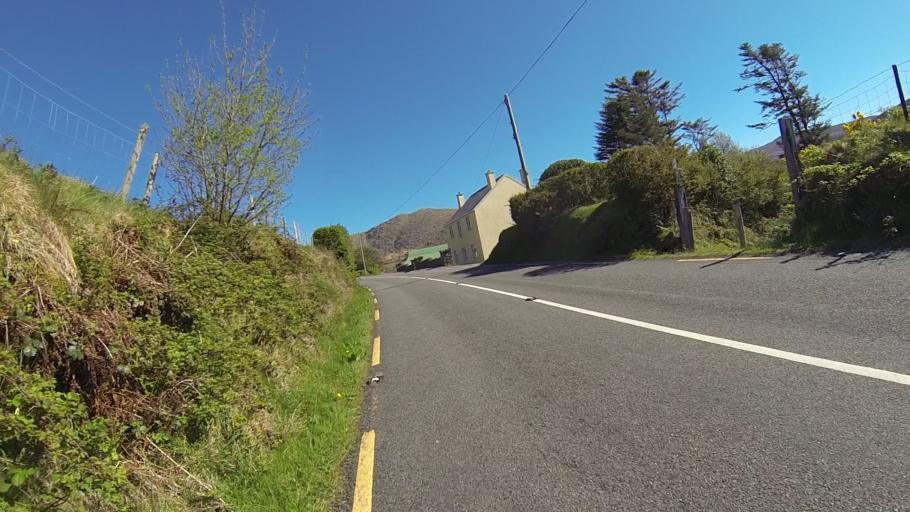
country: IE
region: Munster
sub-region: Ciarrai
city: Kenmare
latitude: 51.7766
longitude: -9.7296
